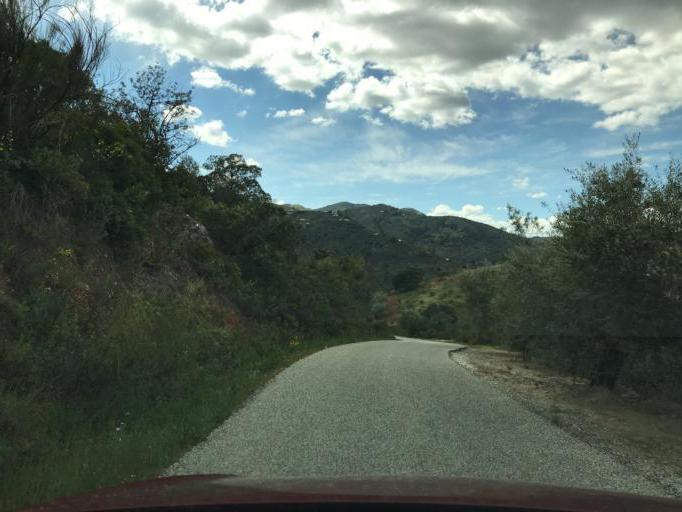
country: ES
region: Andalusia
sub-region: Provincia de Malaga
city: Comares
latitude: 36.8741
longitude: -4.2656
